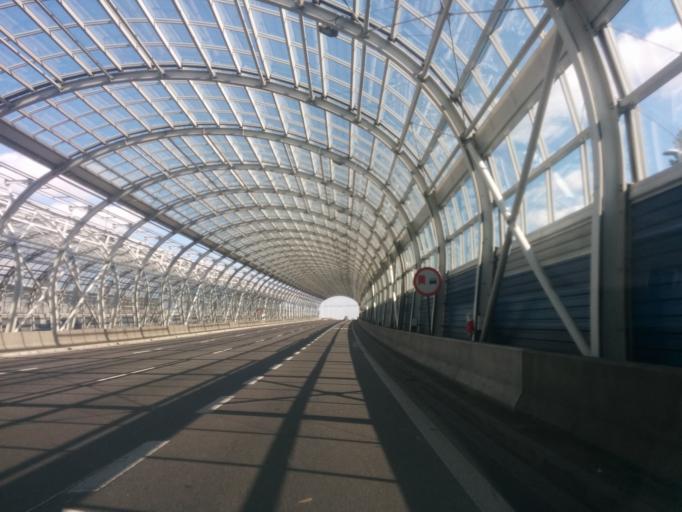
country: PL
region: Masovian Voivodeship
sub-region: Warszawa
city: Targowek
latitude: 52.2983
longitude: 21.0279
